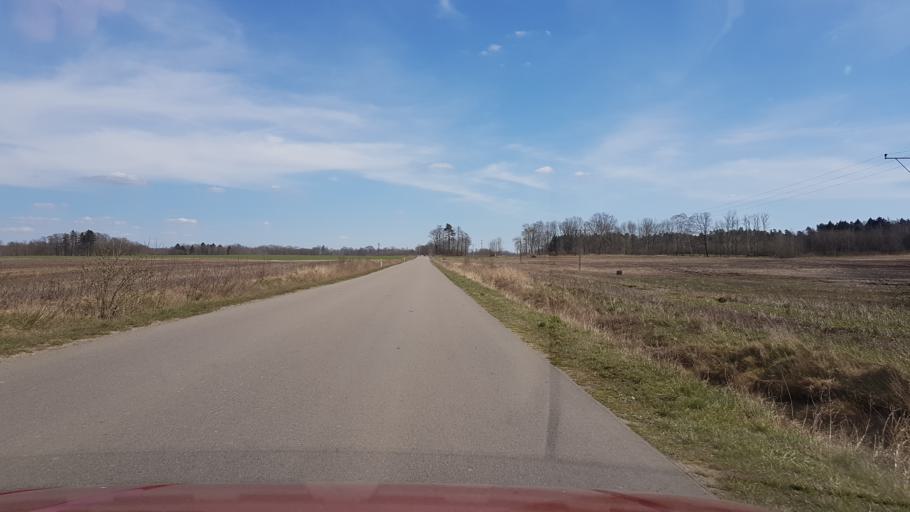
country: PL
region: West Pomeranian Voivodeship
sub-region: Powiat koszalinski
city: Mielno
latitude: 54.1581
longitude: 16.0509
